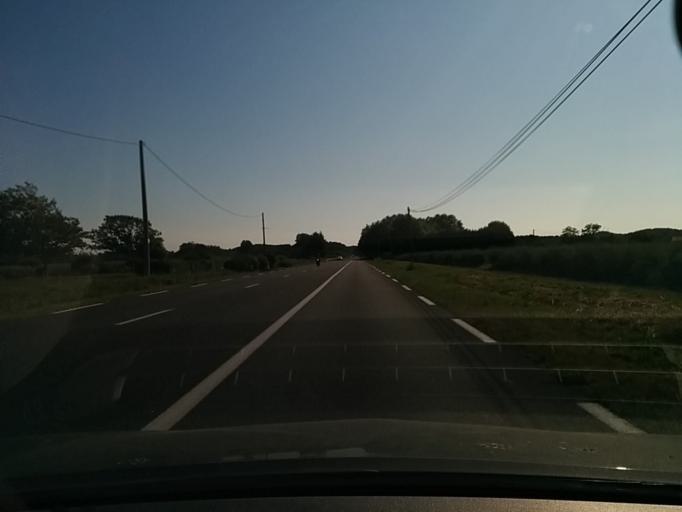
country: FR
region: Aquitaine
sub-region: Departement des Landes
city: Benesse-Maremne
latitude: 43.6219
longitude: -1.3846
